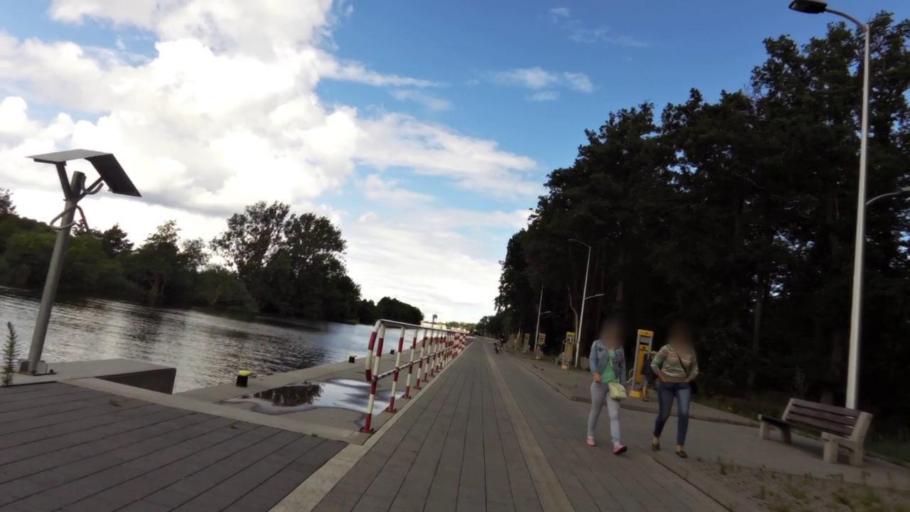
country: PL
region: West Pomeranian Voivodeship
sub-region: Powiat slawienski
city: Darlowo
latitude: 54.4296
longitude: 16.3935
